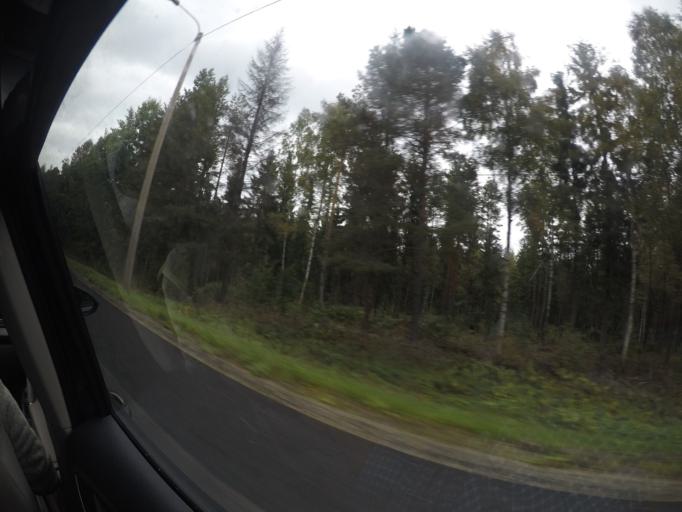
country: FI
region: Pirkanmaa
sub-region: Tampere
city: Kangasala
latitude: 61.4436
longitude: 24.1154
